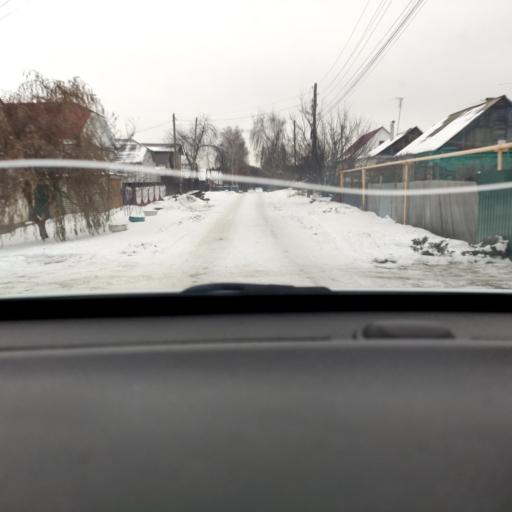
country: RU
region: Voronezj
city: Somovo
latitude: 51.7442
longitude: 39.3602
